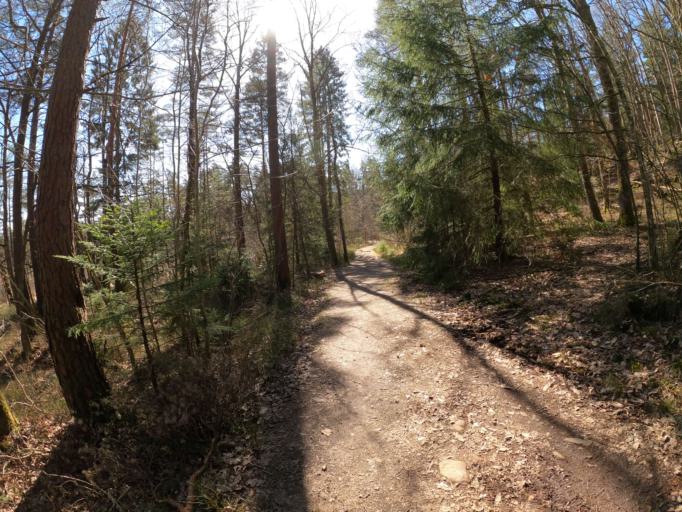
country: SE
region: Vaestra Goetaland
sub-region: Harryda Kommun
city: Molnlycke
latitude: 57.6399
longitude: 12.1289
